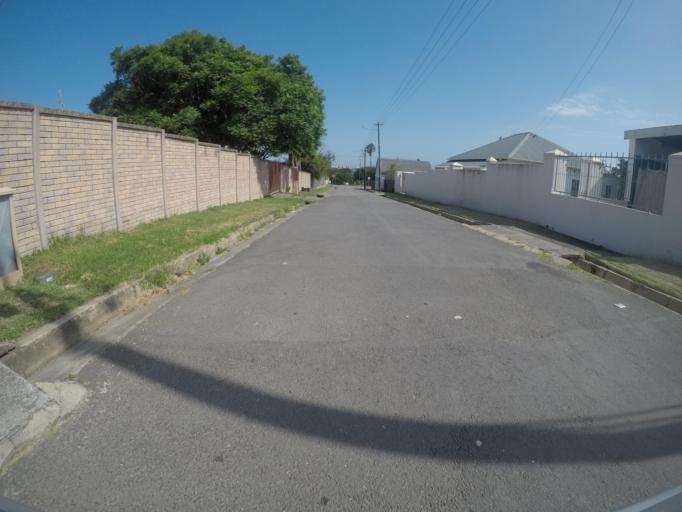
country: ZA
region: Eastern Cape
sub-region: Buffalo City Metropolitan Municipality
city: East London
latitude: -32.9800
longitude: 27.8880
